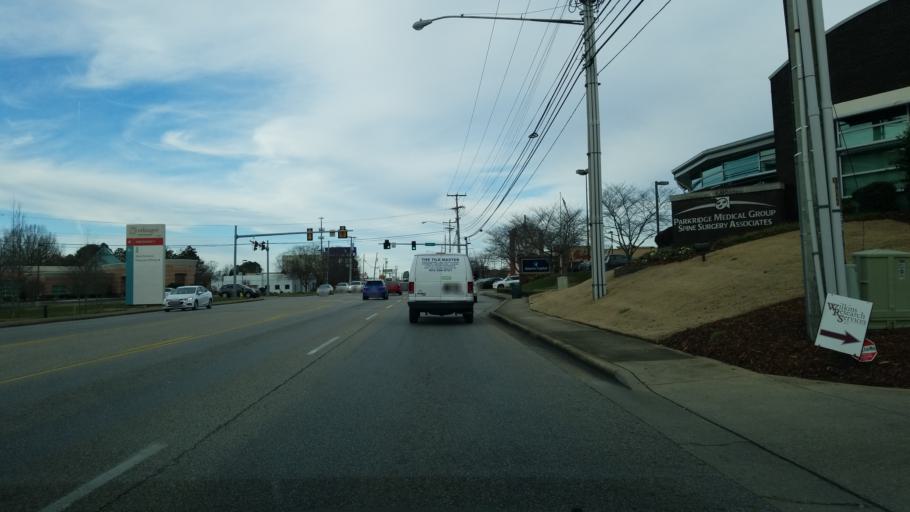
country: US
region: Tennessee
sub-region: Hamilton County
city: East Brainerd
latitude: 35.0228
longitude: -85.1595
